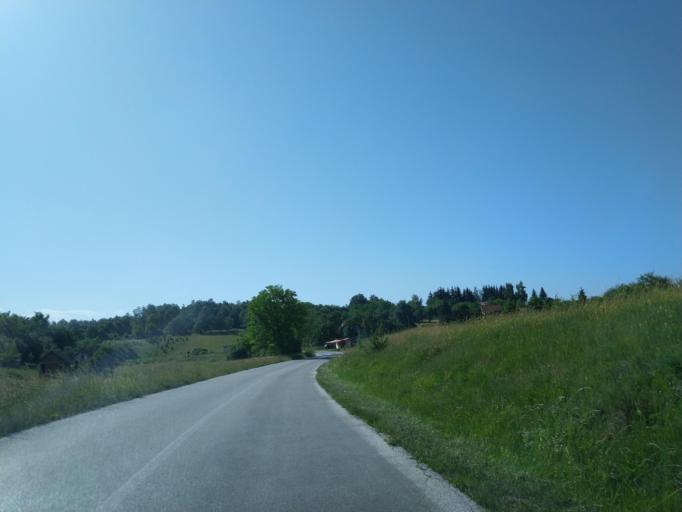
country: RS
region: Central Serbia
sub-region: Zlatiborski Okrug
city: Uzice
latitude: 43.8794
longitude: 19.7487
